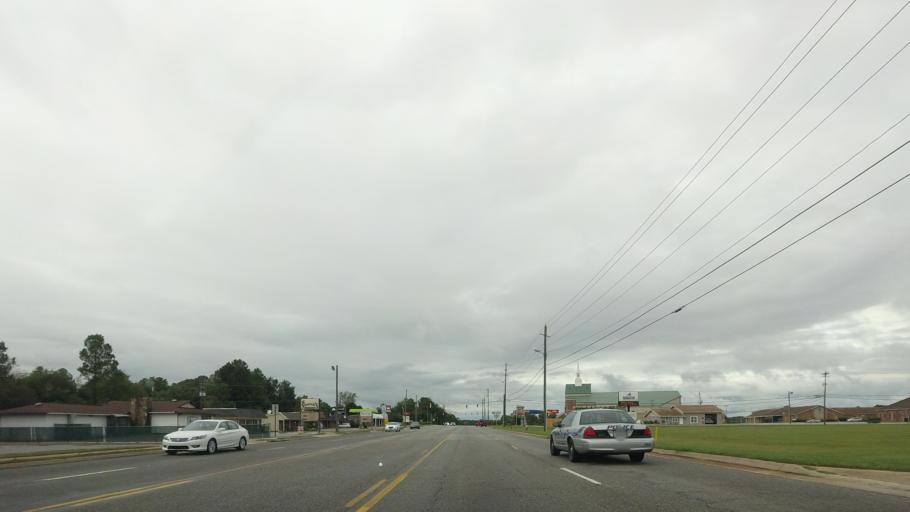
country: US
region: Georgia
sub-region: Houston County
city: Warner Robins
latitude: 32.5770
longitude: -83.6237
